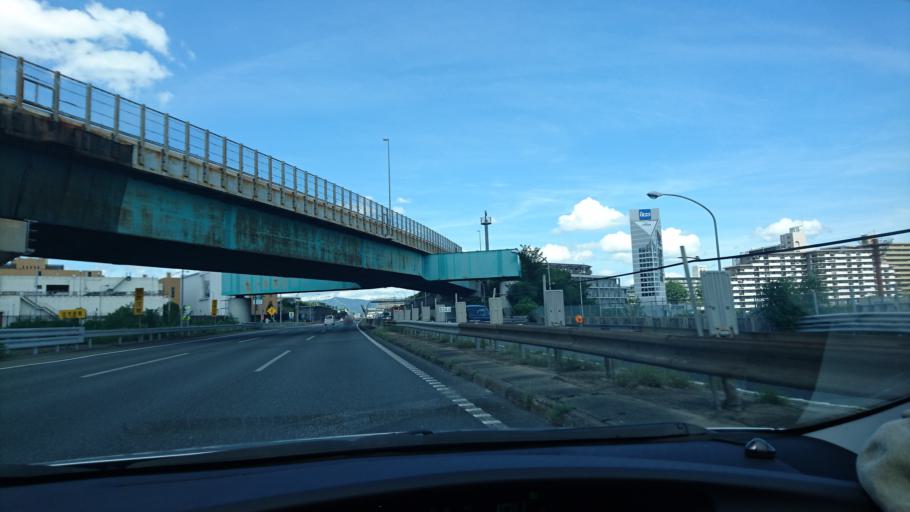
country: JP
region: Osaka
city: Ibaraki
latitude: 34.8083
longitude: 135.5440
